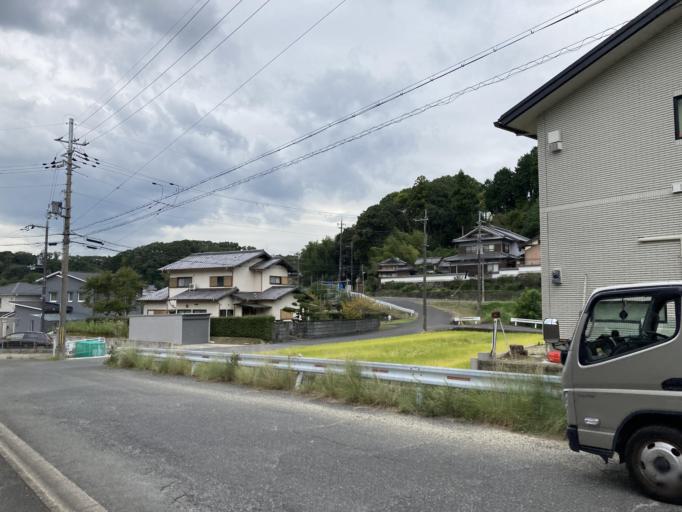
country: JP
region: Nara
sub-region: Ikoma-shi
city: Ikoma
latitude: 34.6821
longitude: 135.6995
